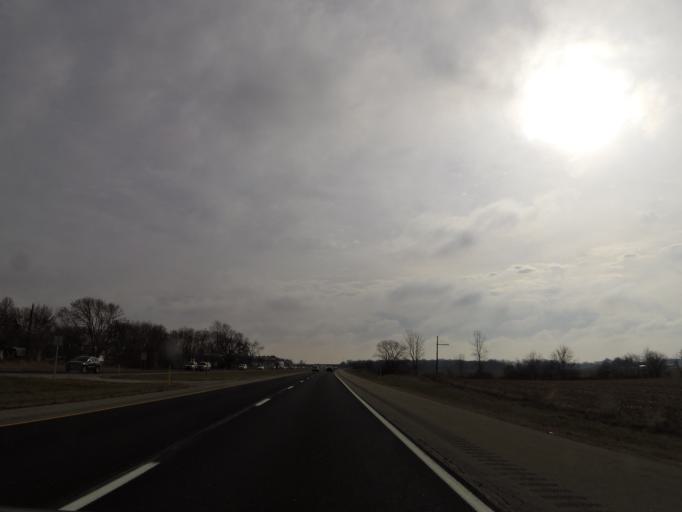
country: US
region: Indiana
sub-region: Hancock County
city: New Palestine
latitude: 39.6681
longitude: -85.9515
